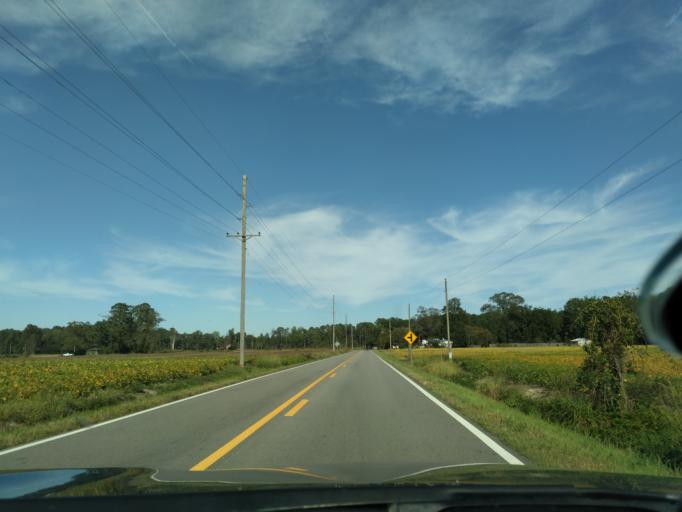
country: US
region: North Carolina
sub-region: Beaufort County
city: River Road
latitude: 35.5144
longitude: -76.9632
